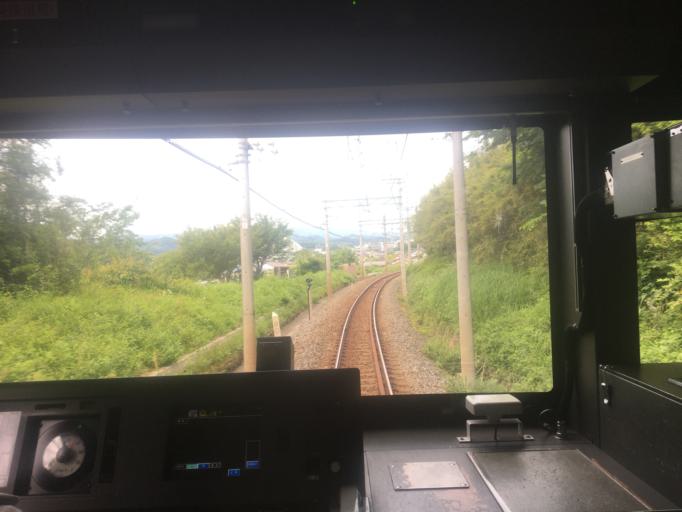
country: JP
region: Saitama
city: Ogawa
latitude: 36.0526
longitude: 139.2837
